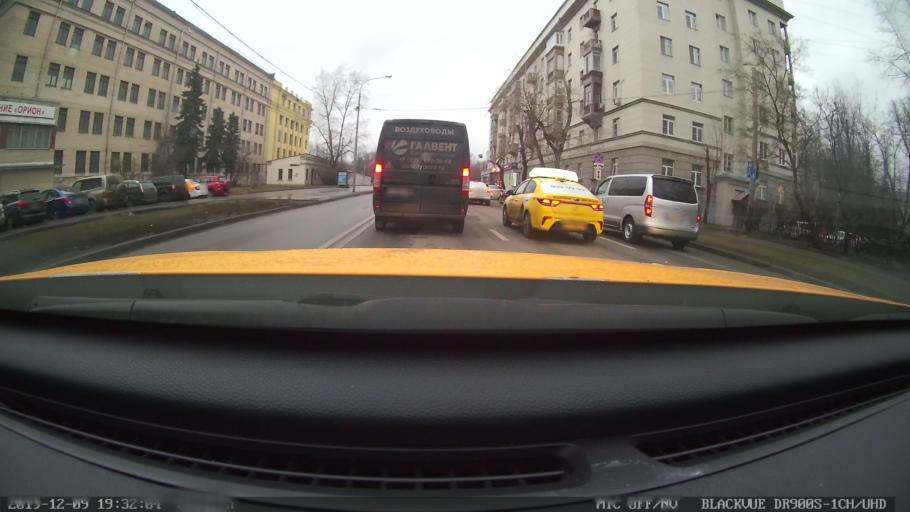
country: RU
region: Moscow
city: Ryazanskiy
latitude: 55.7574
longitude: 37.7577
